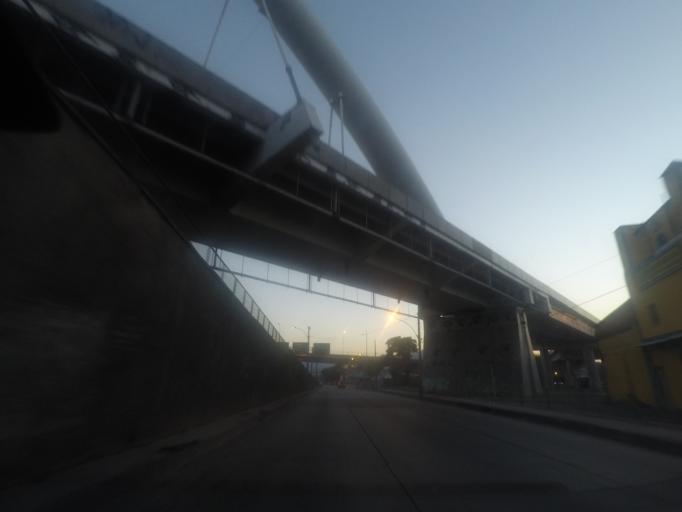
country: BR
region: Rio de Janeiro
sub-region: Rio De Janeiro
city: Rio de Janeiro
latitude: -22.8500
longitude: -43.2477
